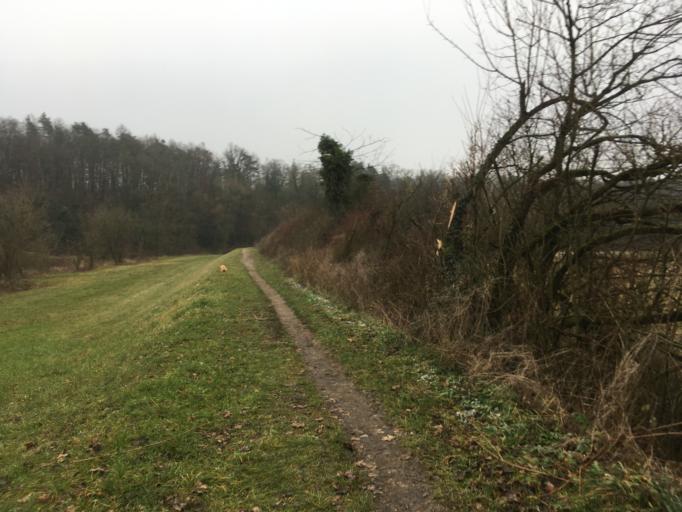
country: CH
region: Aargau
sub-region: Bezirk Zurzach
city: Koblenz
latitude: 47.6217
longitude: 8.2594
